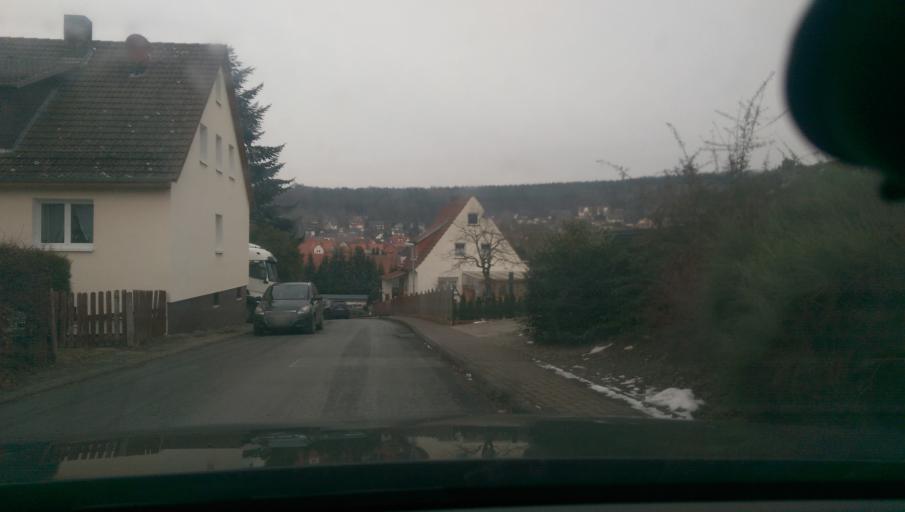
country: DE
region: Hesse
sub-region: Regierungsbezirk Kassel
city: Nieste
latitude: 51.3106
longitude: 9.6682
